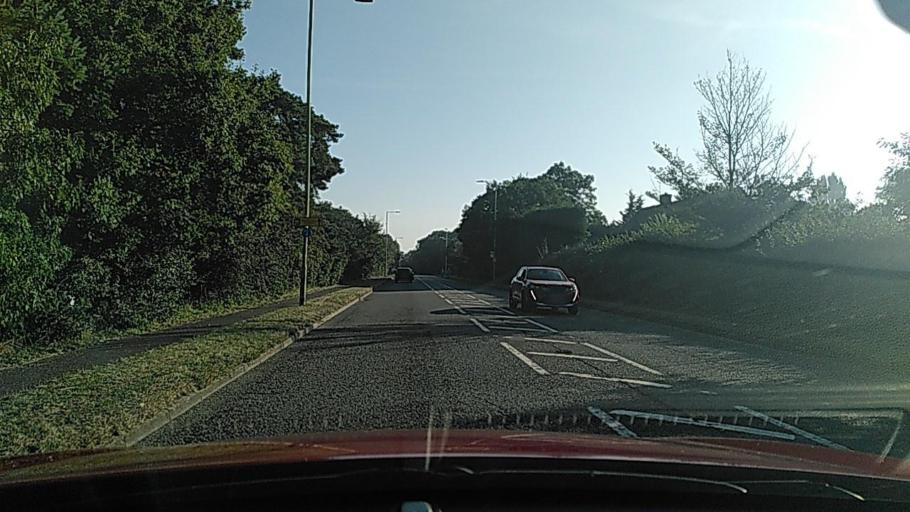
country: GB
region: England
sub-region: Wokingham
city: Sonning
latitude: 51.4651
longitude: -0.9107
